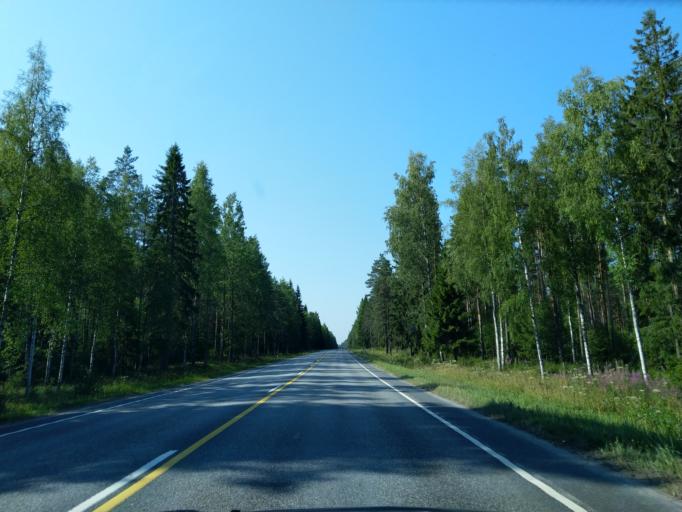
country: FI
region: Satakunta
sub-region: Pori
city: Pomarkku
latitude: 61.6565
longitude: 21.9647
